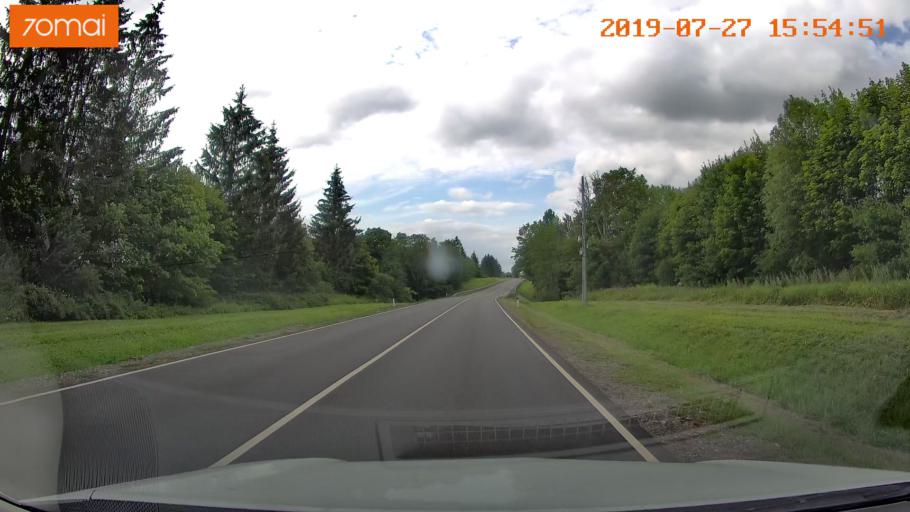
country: RU
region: Kaliningrad
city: Chernyakhovsk
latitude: 54.6100
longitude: 21.9314
